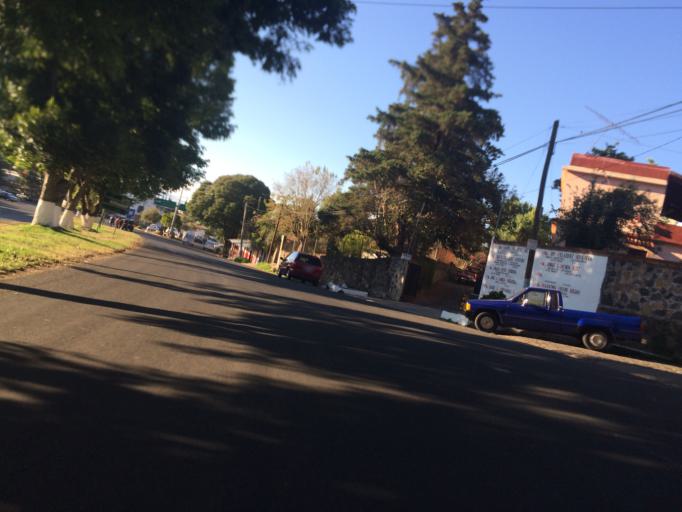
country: MX
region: Michoacan
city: Patzcuaro
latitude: 19.5073
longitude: -101.6131
